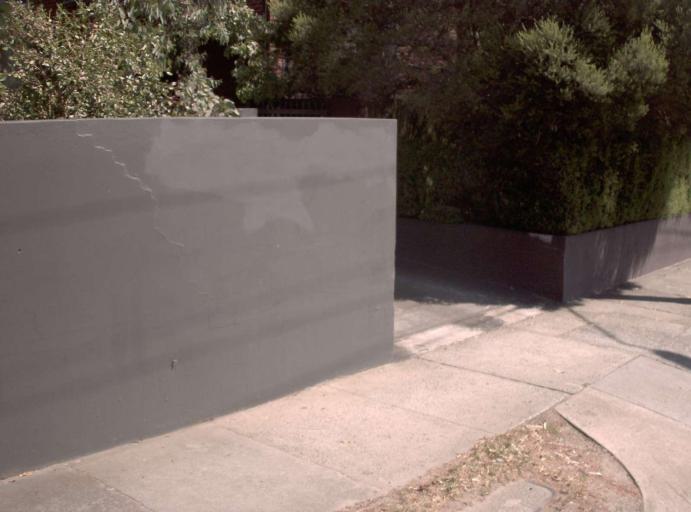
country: AU
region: Victoria
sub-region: Monash
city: Chadstone
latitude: -37.8915
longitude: 145.0884
